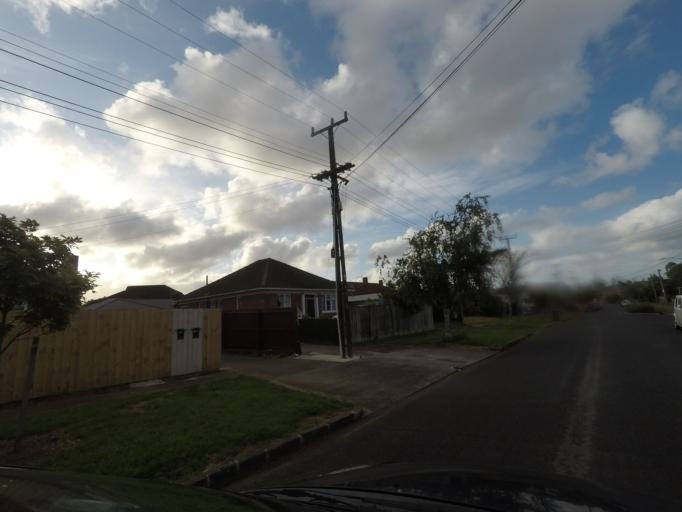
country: NZ
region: Auckland
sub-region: Auckland
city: Auckland
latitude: -36.9091
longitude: 174.7429
